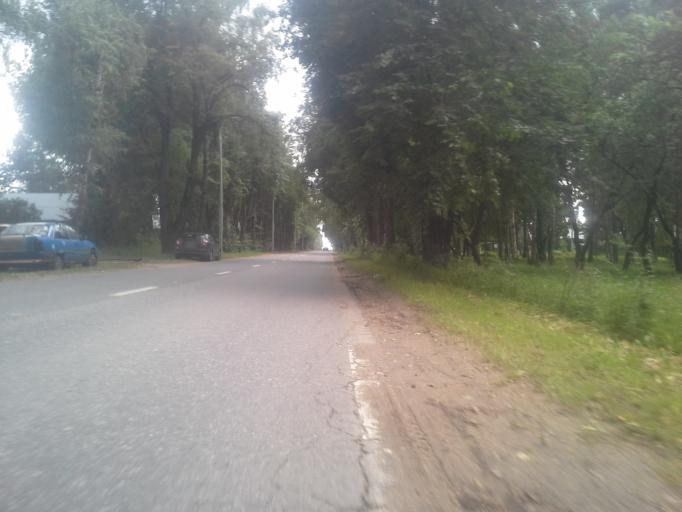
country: RU
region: Moskovskaya
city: Zvenigorod
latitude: 55.7249
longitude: 36.8318
